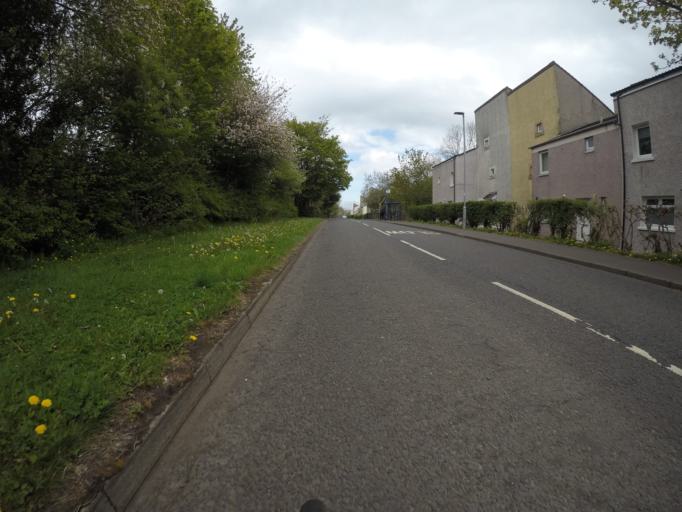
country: GB
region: Scotland
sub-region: North Ayrshire
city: Irvine
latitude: 55.6280
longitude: -4.6318
